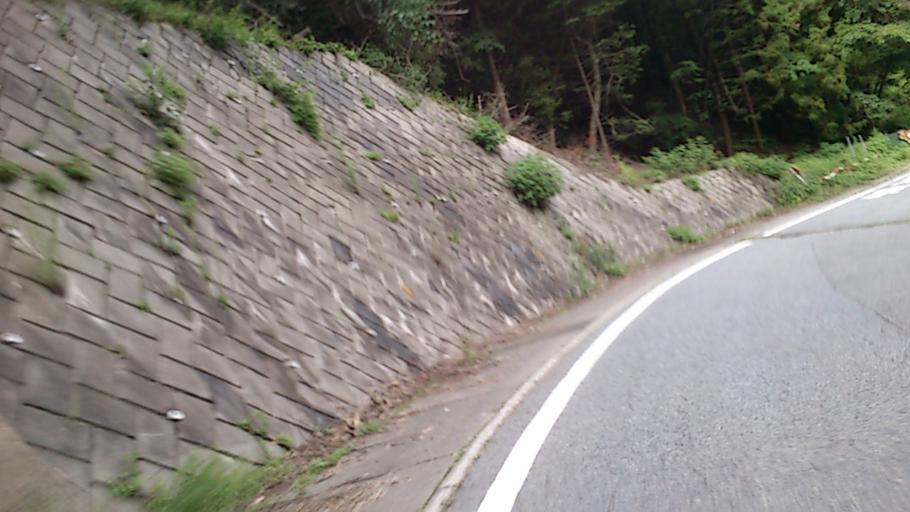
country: JP
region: Nagano
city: Saku
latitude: 36.2245
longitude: 138.6193
